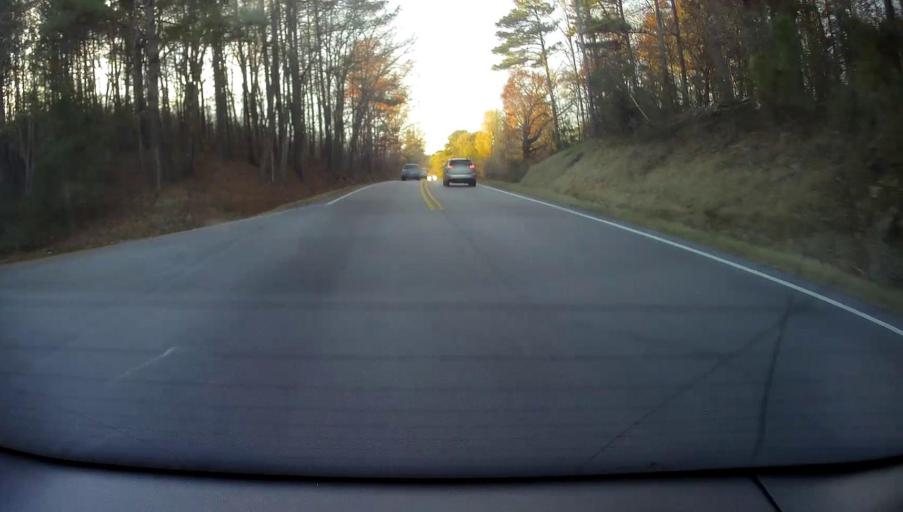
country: US
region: Alabama
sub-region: Saint Clair County
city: Steele
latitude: 34.0666
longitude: -86.2616
